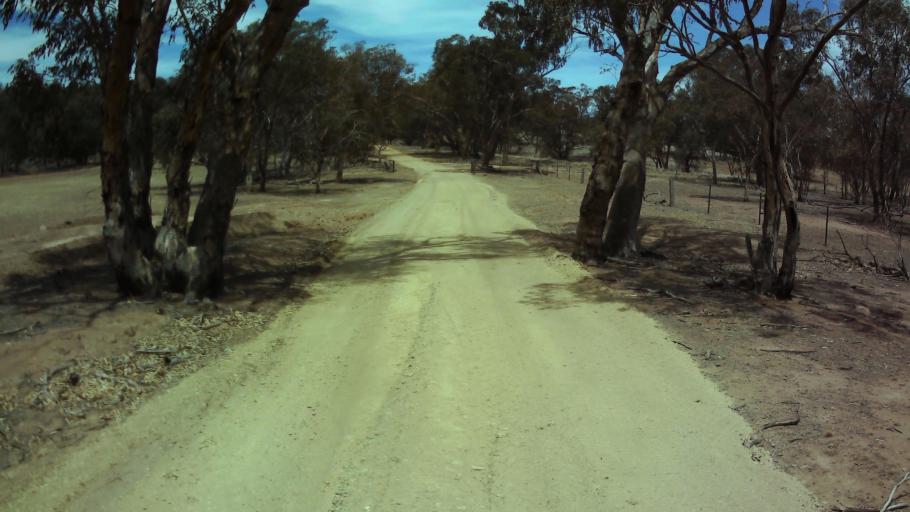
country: AU
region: New South Wales
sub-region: Weddin
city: Grenfell
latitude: -33.7856
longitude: 148.1534
